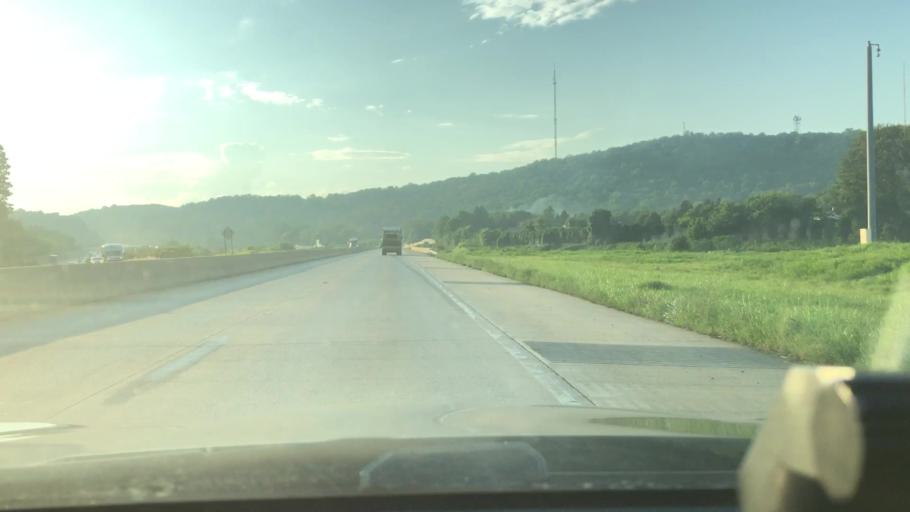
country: US
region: Pennsylvania
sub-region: Lehigh County
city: Coopersburg
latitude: 40.5534
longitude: -75.4303
